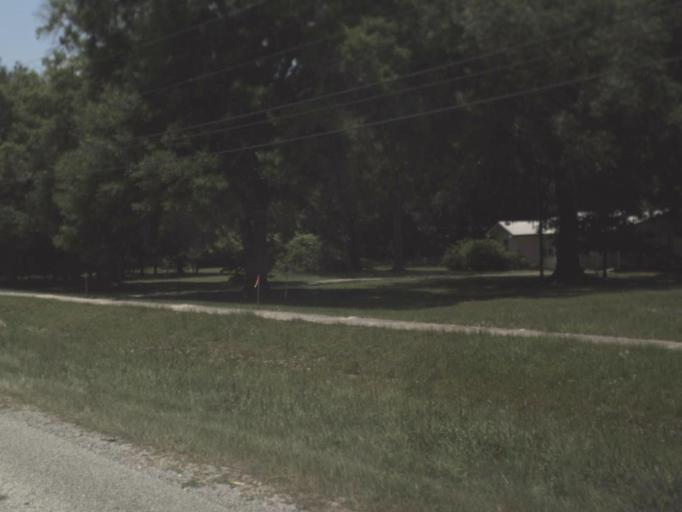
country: US
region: Florida
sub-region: Bradford County
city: Starke
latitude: 29.9303
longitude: -82.1200
